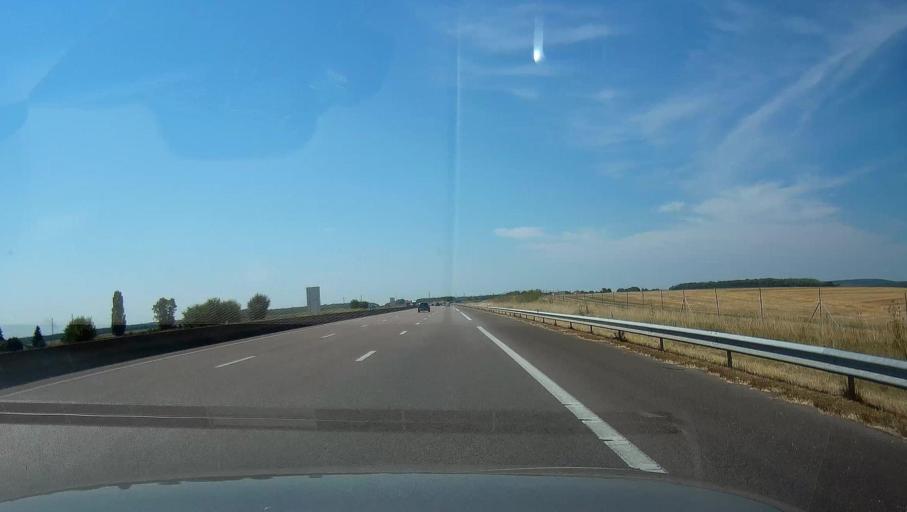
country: FR
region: Bourgogne
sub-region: Departement de la Cote-d'Or
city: Nuits-Saint-Georges
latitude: 47.0943
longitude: 4.9417
